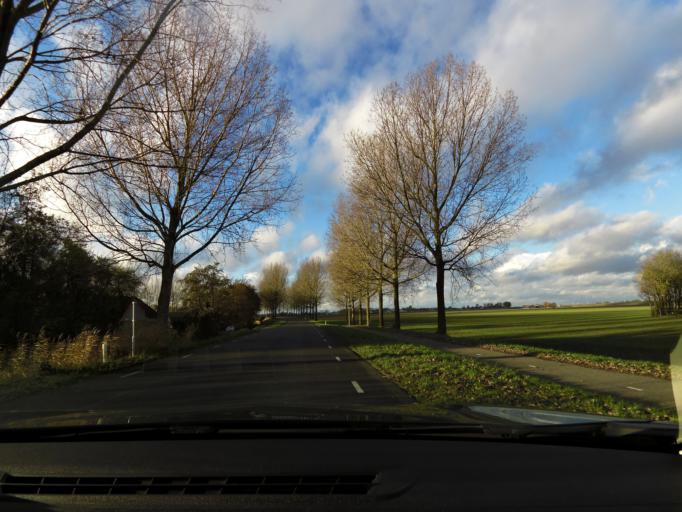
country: NL
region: South Holland
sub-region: Gemeente Goeree-Overflakkee
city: Middelharnis
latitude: 51.7241
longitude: 4.2517
